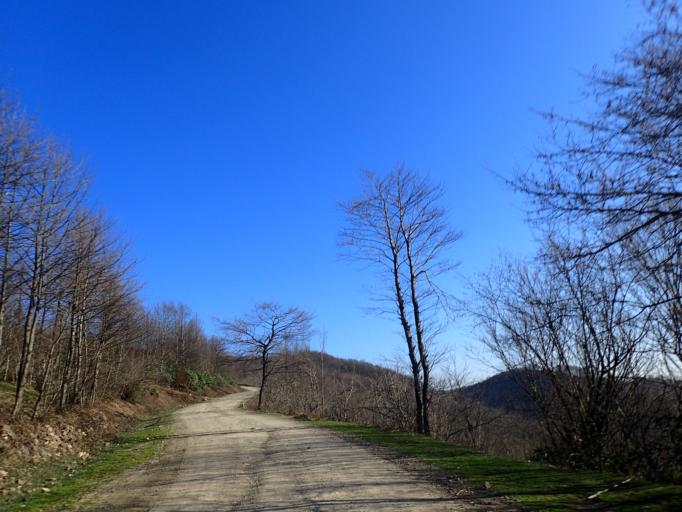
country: TR
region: Ordu
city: Camas
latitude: 40.8611
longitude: 37.5010
